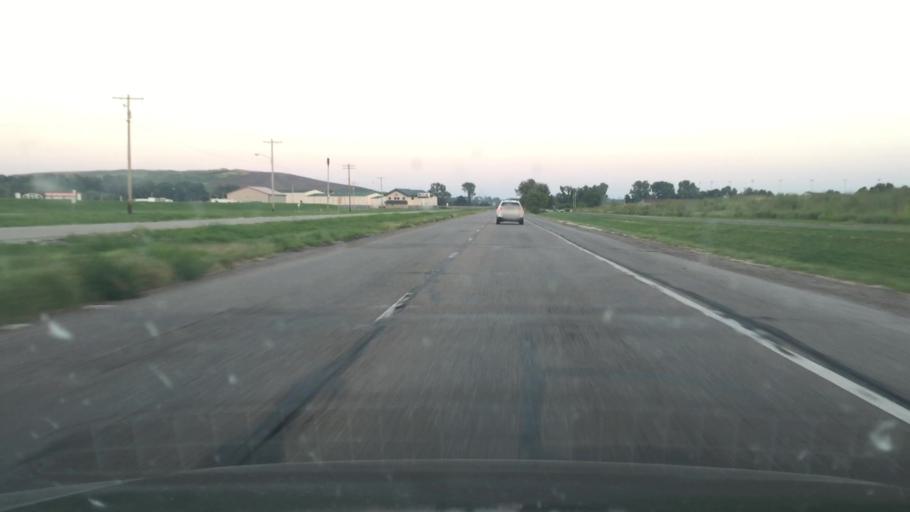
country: US
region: Illinois
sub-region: Madison County
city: Madison
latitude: 38.6631
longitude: -90.1414
